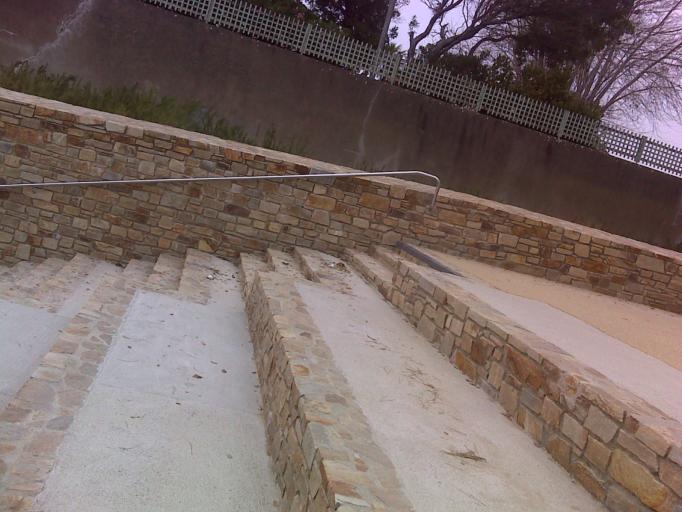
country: FR
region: Pays de la Loire
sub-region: Departement de la Loire-Atlantique
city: La Bernerie-en-Retz
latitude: 47.0807
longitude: -2.0402
